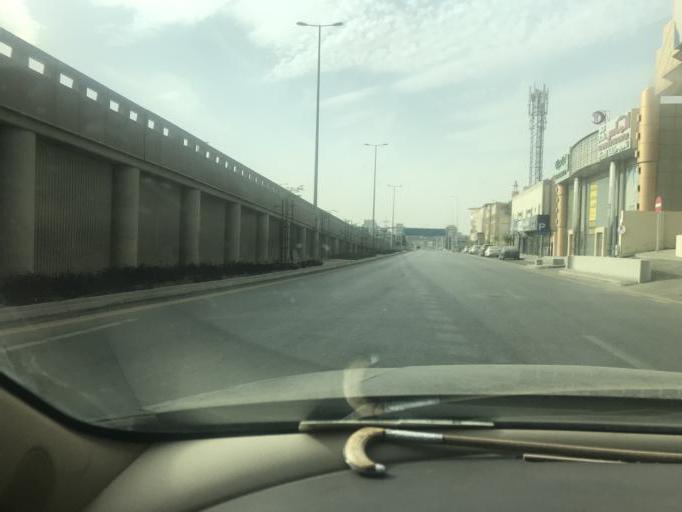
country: SA
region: Ar Riyad
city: Riyadh
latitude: 24.7768
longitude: 46.6652
